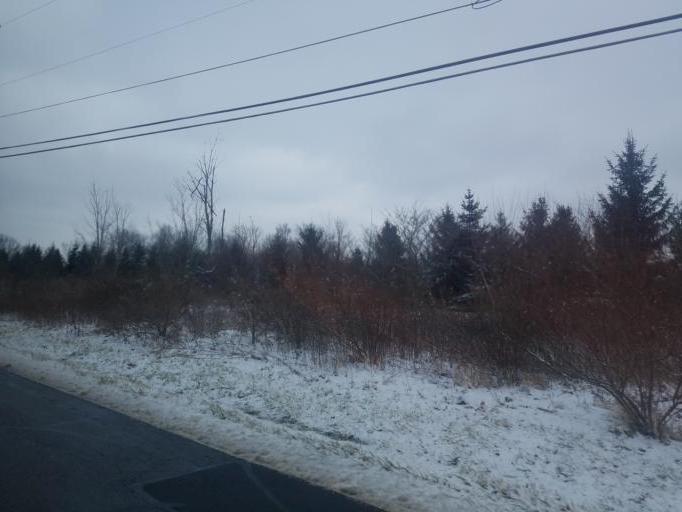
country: US
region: Ohio
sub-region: Franklin County
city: New Albany
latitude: 40.0963
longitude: -82.7782
